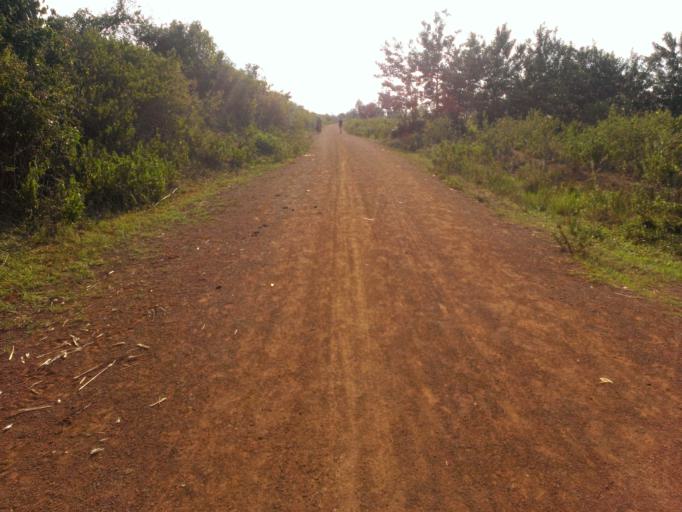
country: UG
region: Eastern Region
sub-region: Busia District
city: Busia
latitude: 0.5504
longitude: 33.9931
